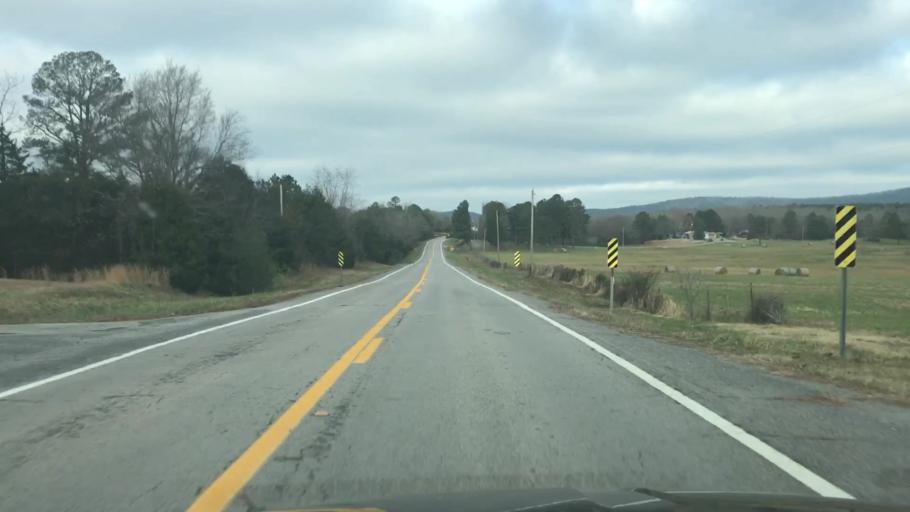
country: US
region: Arkansas
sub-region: Montgomery County
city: Mount Ida
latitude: 34.6491
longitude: -93.7513
